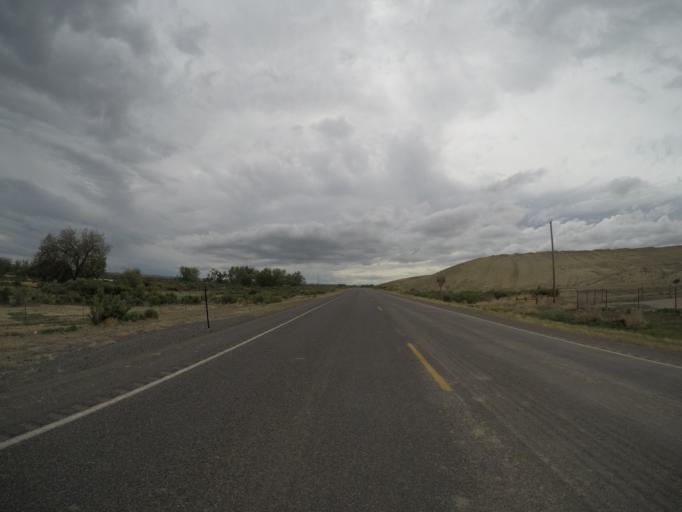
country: US
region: Wyoming
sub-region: Big Horn County
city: Lovell
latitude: 44.8749
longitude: -108.3098
